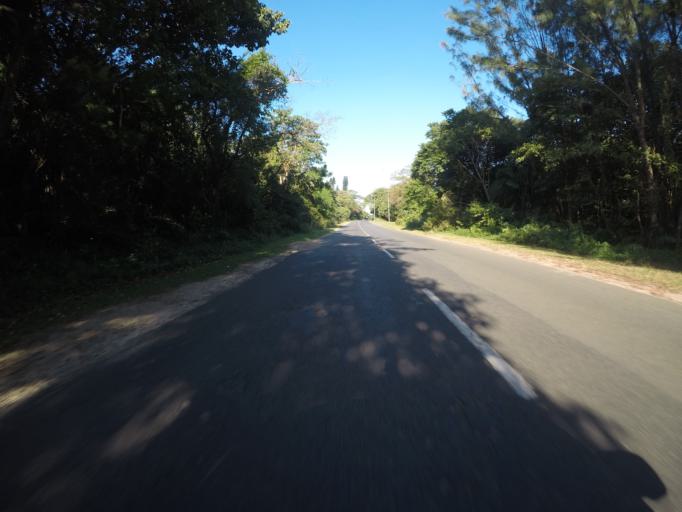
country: ZA
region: KwaZulu-Natal
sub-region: uThungulu District Municipality
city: Richards Bay
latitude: -28.7921
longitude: 32.0916
